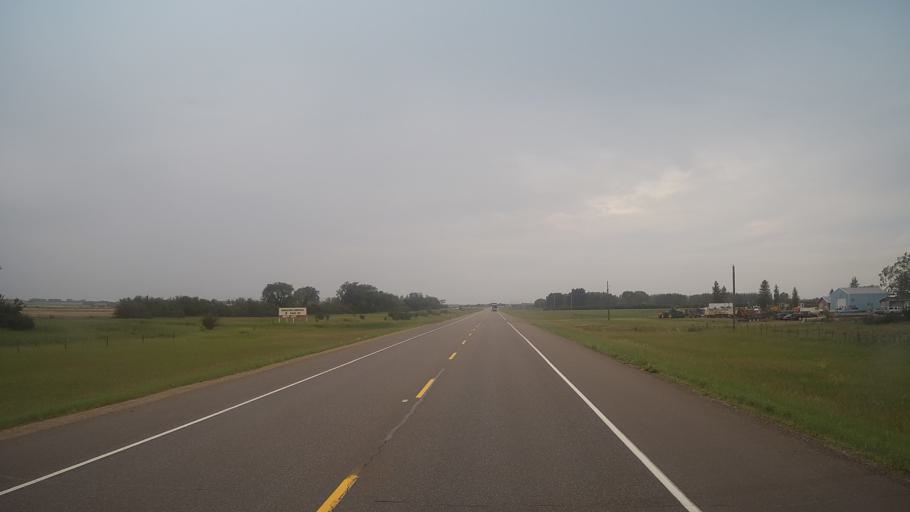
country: CA
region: Saskatchewan
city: Dalmeny
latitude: 52.1292
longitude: -106.8709
